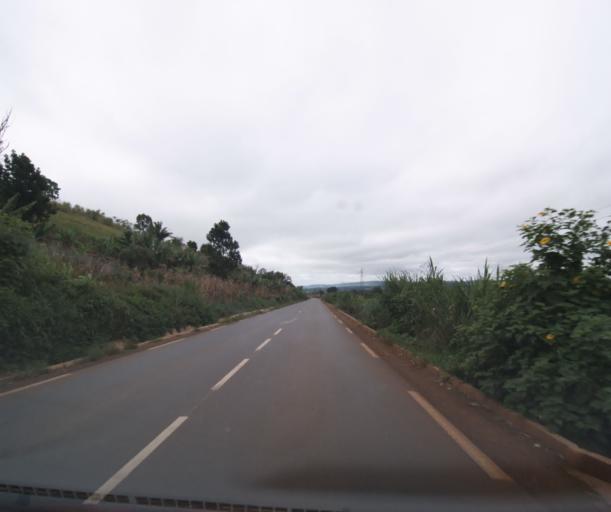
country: CM
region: West
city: Bansoa
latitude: 5.5490
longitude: 10.3277
